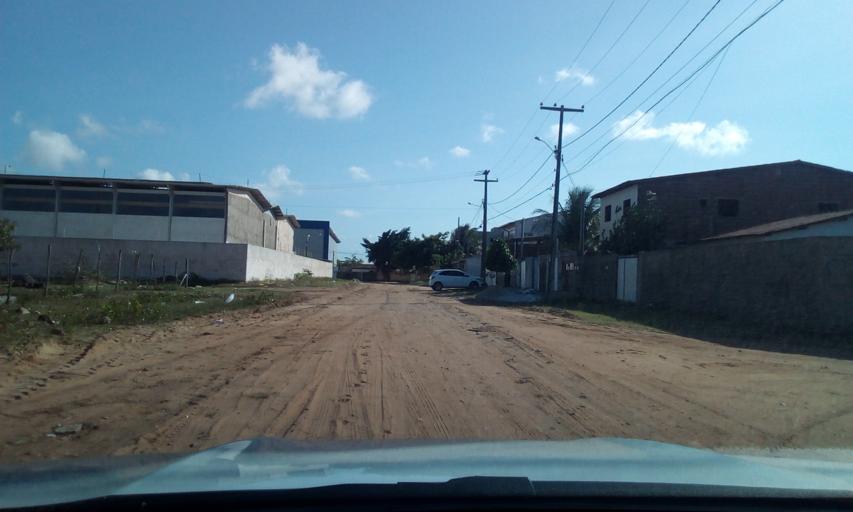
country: BR
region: Paraiba
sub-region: Cabedelo
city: Cabedelo
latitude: -7.0334
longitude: -34.8443
